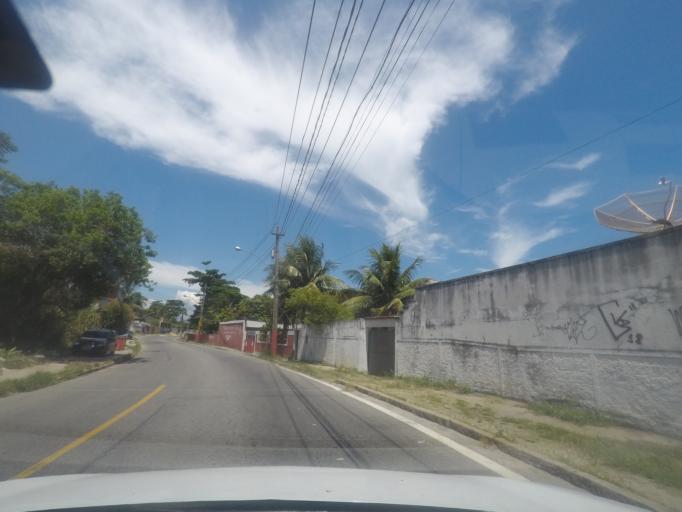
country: BR
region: Rio de Janeiro
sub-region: Itaguai
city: Itaguai
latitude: -22.9858
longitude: -43.6999
